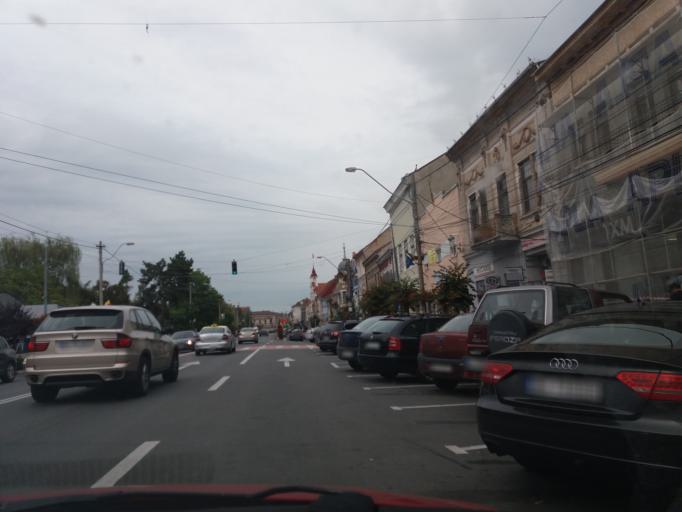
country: RO
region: Mures
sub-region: Municipiul Reghin
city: Reghin
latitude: 46.7801
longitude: 24.7005
